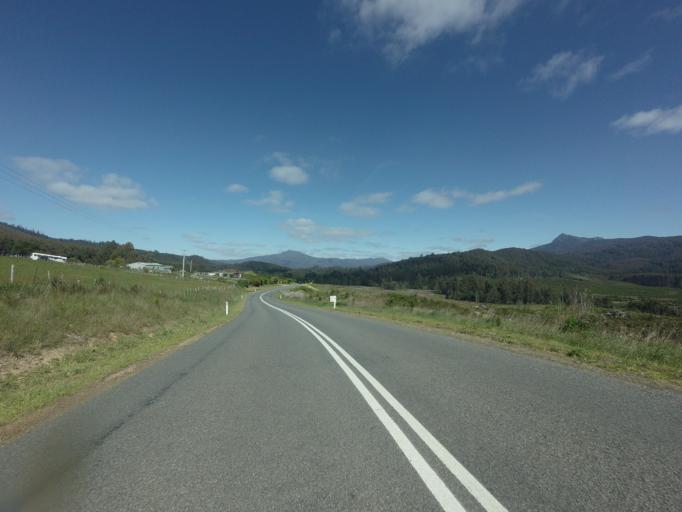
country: AU
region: Tasmania
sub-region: Derwent Valley
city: New Norfolk
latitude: -42.7512
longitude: 146.6392
